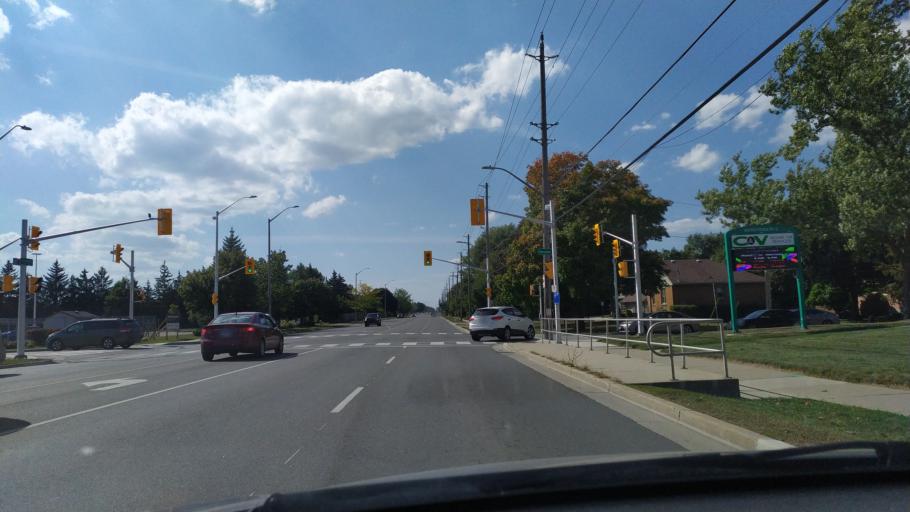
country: CA
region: Ontario
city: London
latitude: 42.9432
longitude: -81.2297
